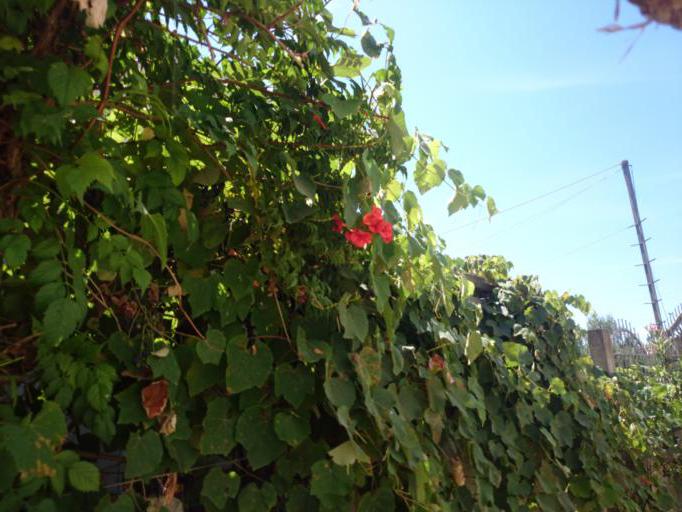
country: AL
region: Tirane
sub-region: Rrethi i Kavajes
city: Synej
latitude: 41.1811
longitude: 19.5455
